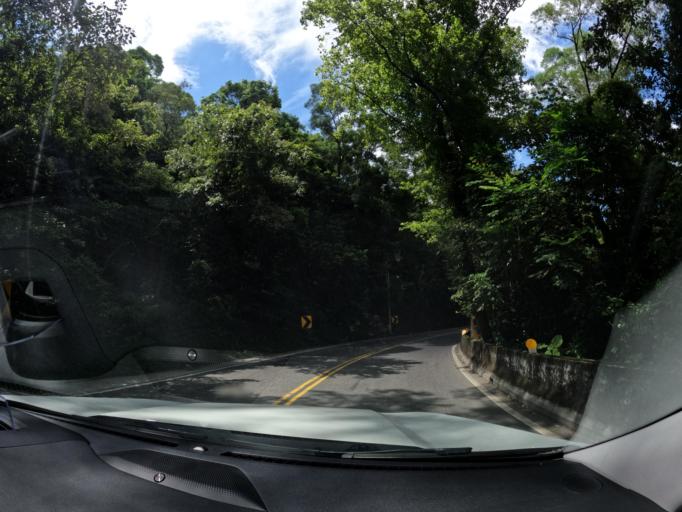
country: TW
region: Taipei
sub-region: Taipei
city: Banqiao
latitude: 25.1139
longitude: 121.3863
